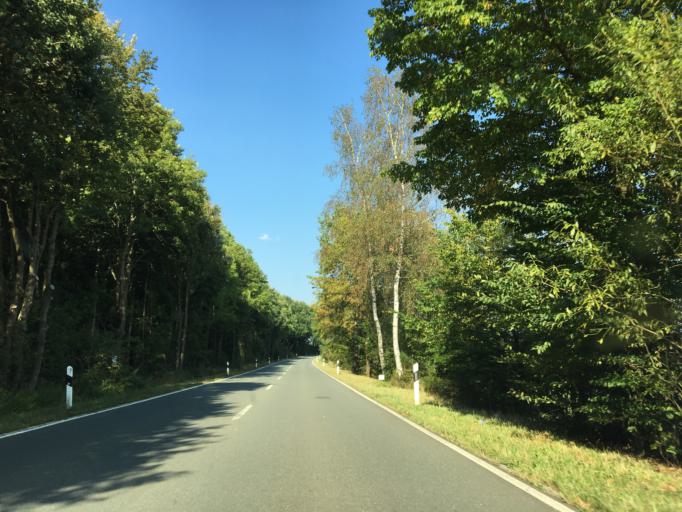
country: DE
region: Hesse
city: Frankenberg
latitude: 51.0286
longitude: 8.7807
